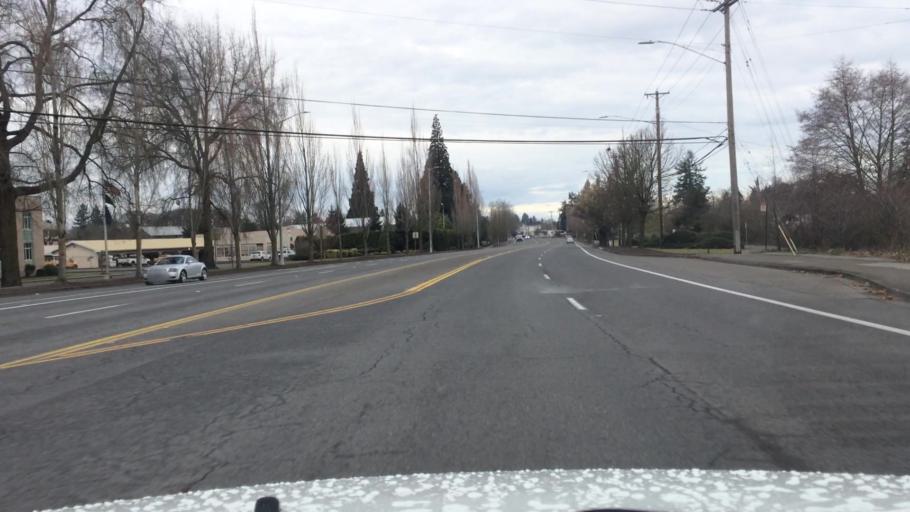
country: US
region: Oregon
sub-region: Marion County
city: Four Corners
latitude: 44.9292
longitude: -123.0036
